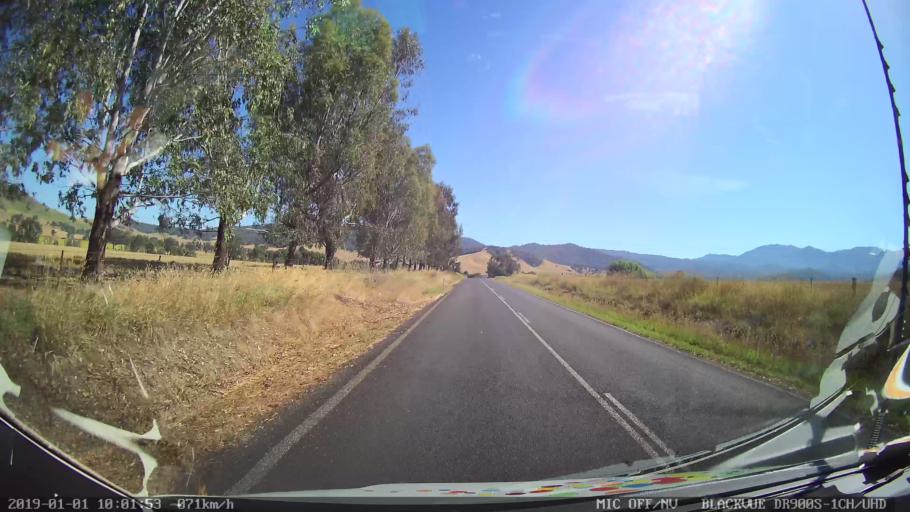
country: AU
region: New South Wales
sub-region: Snowy River
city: Jindabyne
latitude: -36.1868
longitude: 148.1010
